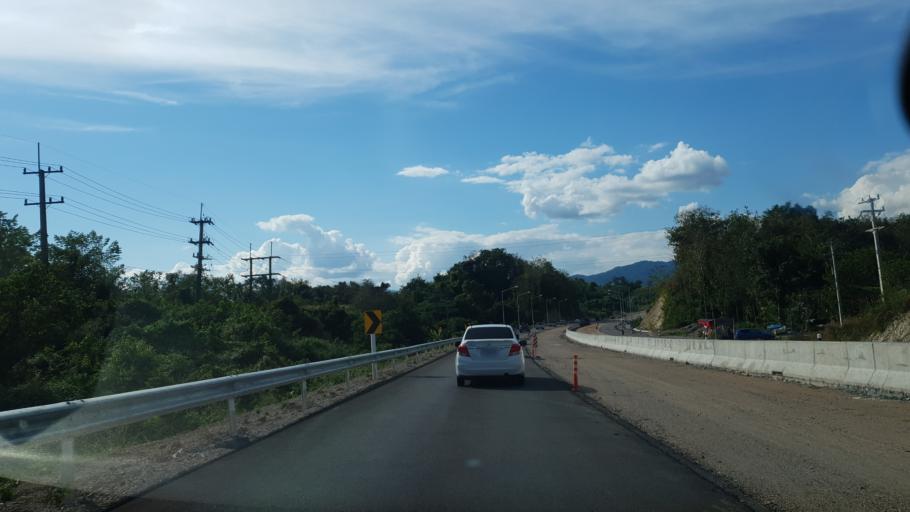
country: TH
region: Phrae
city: Long
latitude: 18.0027
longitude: 99.7434
